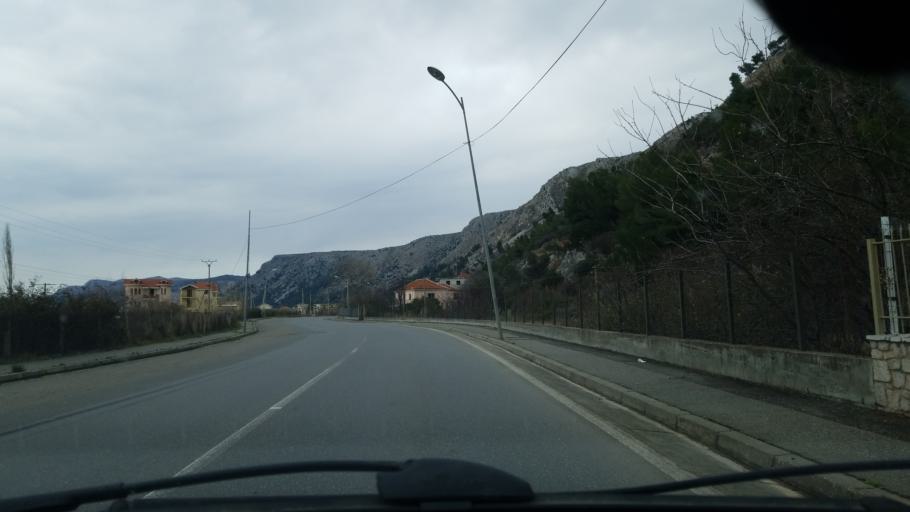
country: AL
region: Lezhe
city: Lezhe
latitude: 41.7926
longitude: 19.6228
